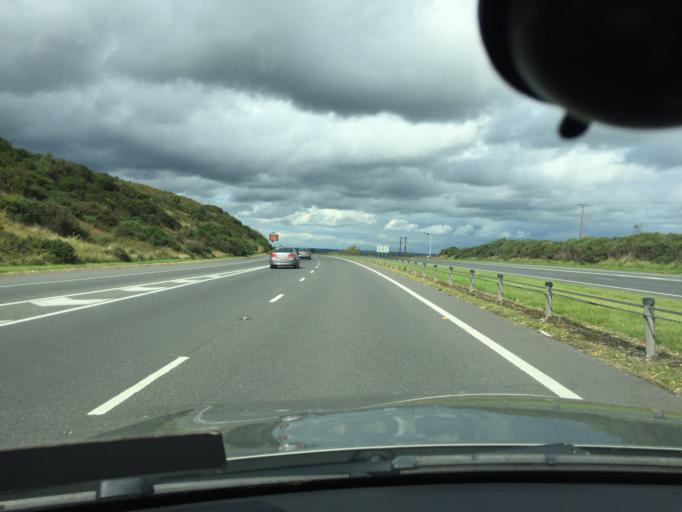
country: GB
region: Northern Ireland
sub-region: Newry and Mourne District
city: Newry
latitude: 54.1410
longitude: -6.3430
